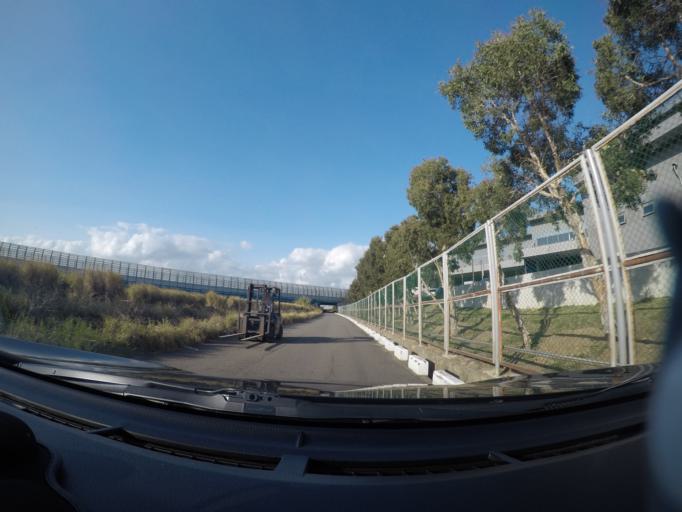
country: TW
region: Taiwan
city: Taoyuan City
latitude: 25.0975
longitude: 121.2515
